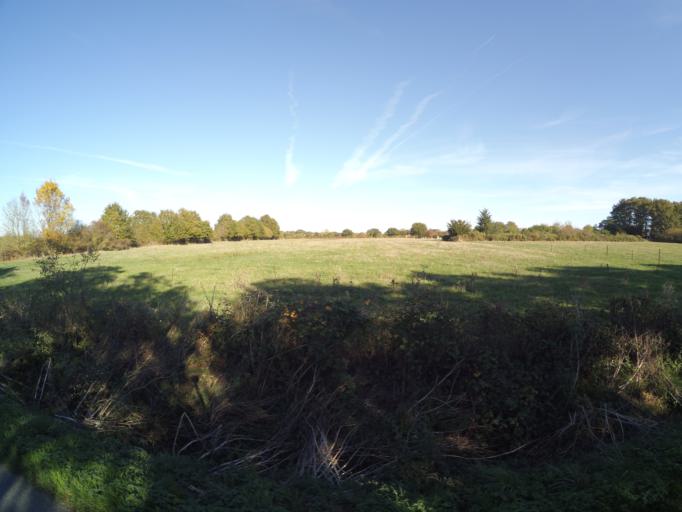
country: FR
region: Pays de la Loire
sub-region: Departement de la Loire-Atlantique
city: Saint-Lumine-de-Clisson
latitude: 47.0790
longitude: -1.3303
